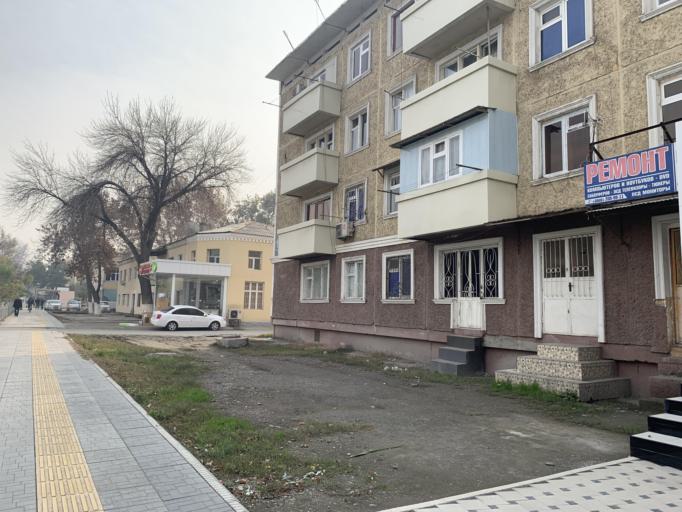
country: UZ
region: Fergana
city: Qo`qon
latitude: 40.5454
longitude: 70.9303
